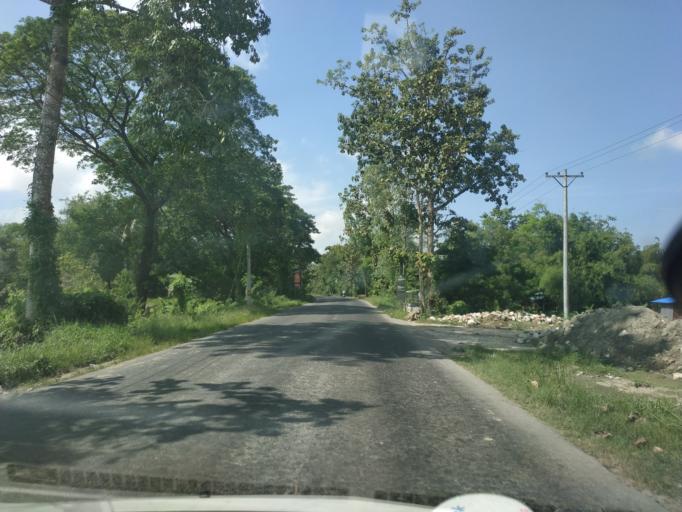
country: MM
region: Ayeyarwady
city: Nyaungdon
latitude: 17.0455
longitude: 95.5461
